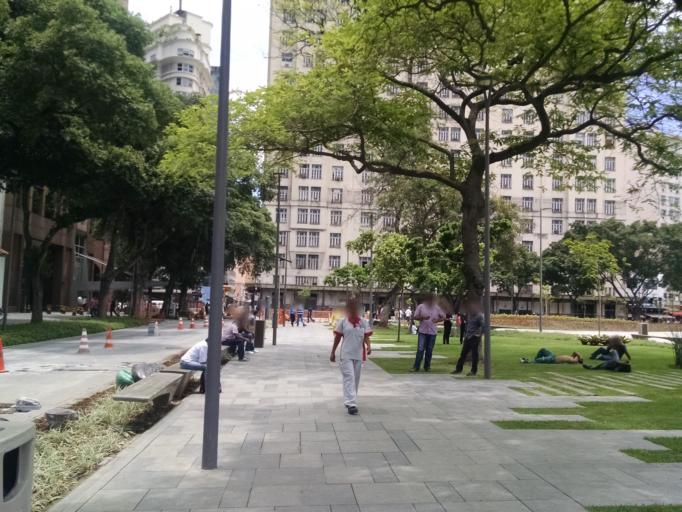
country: BR
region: Rio de Janeiro
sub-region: Rio De Janeiro
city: Rio de Janeiro
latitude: -22.8963
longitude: -43.1804
